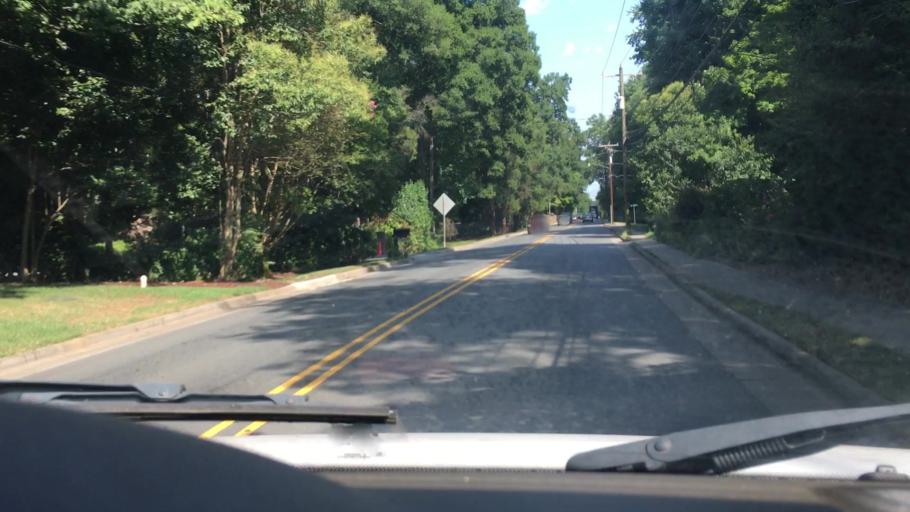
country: US
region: North Carolina
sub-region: Gaston County
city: Davidson
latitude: 35.4944
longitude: -80.8366
